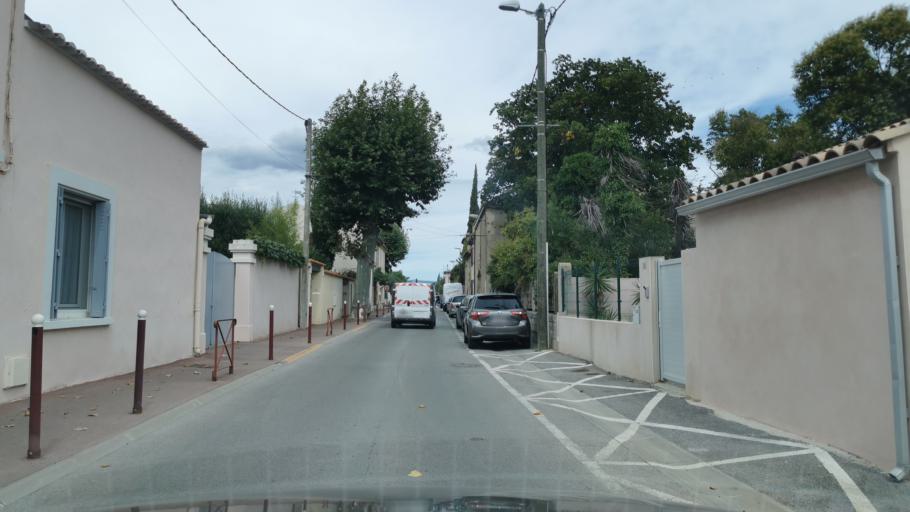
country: FR
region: Languedoc-Roussillon
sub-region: Departement de l'Aude
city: Saint-Marcel-sur-Aude
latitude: 43.2593
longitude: 2.9452
